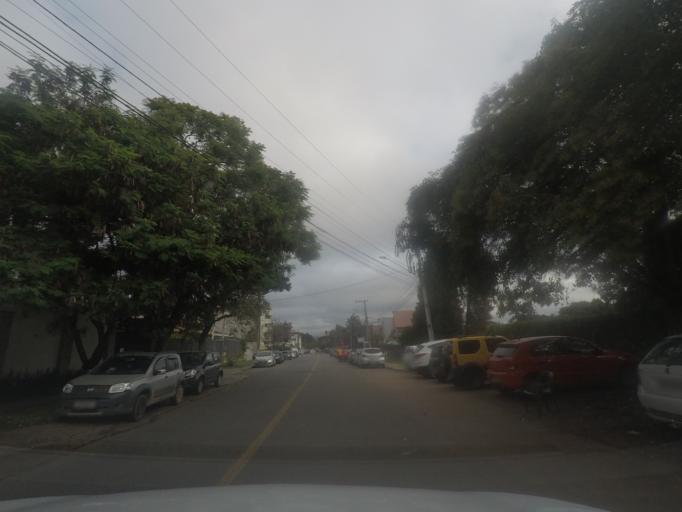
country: BR
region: Parana
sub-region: Curitiba
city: Curitiba
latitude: -25.4236
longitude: -49.2472
